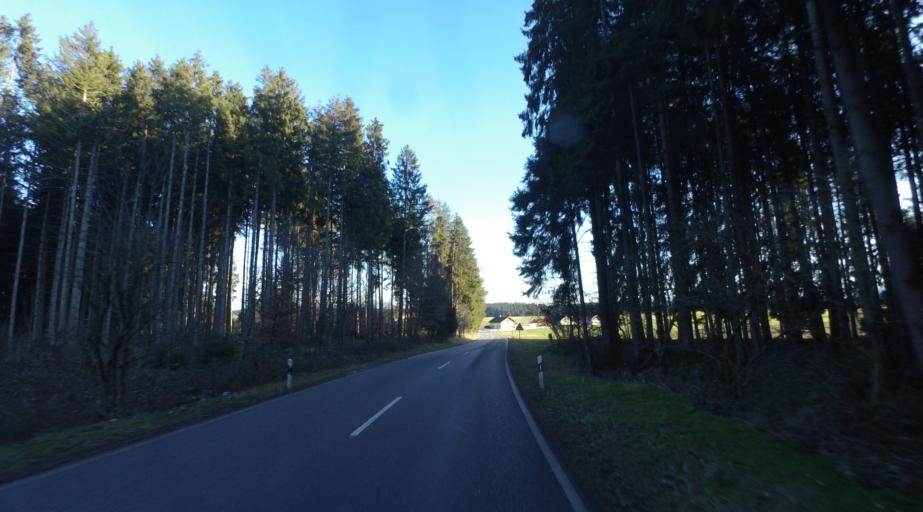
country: DE
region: Bavaria
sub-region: Upper Bavaria
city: Trostberg an der Alz
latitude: 48.0215
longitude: 12.5816
